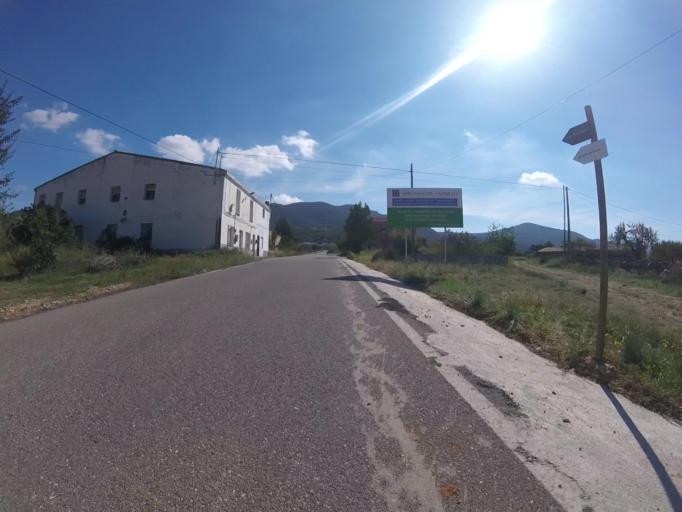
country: ES
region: Valencia
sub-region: Provincia de Castello
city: Sierra-Engarceran
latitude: 40.2978
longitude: -0.0463
